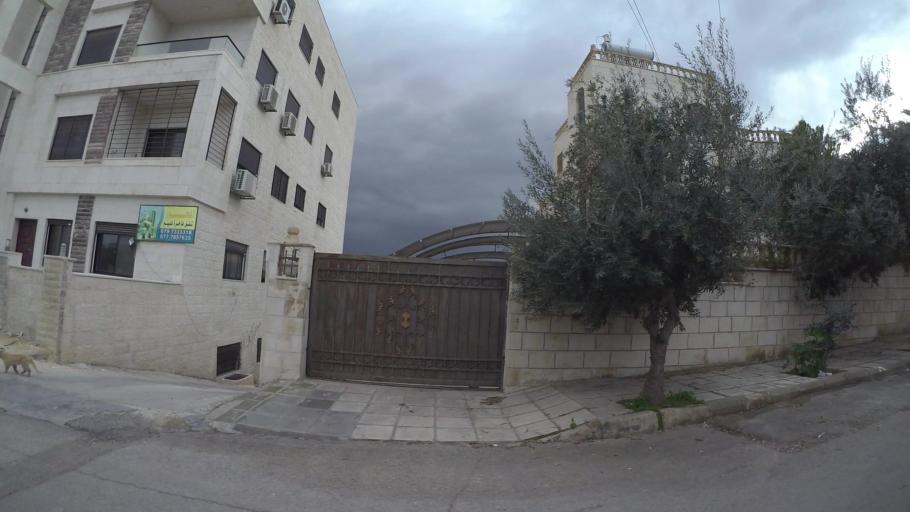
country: JO
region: Amman
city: Amman
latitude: 32.0048
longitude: 35.9450
